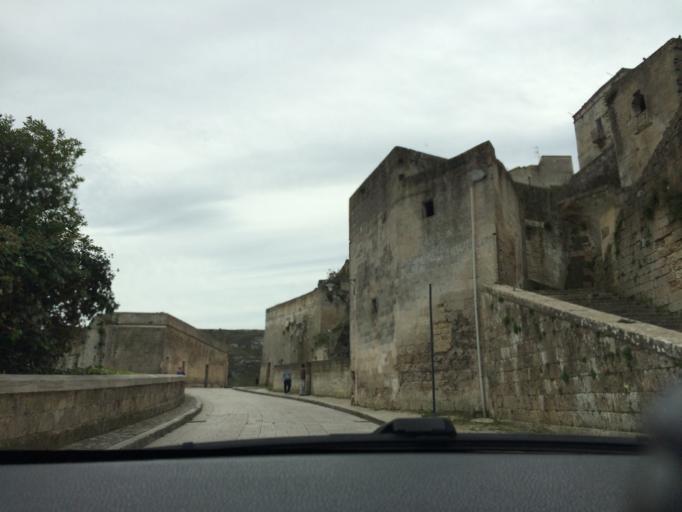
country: IT
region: Basilicate
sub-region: Provincia di Matera
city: Matera
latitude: 40.6675
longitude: 16.6125
